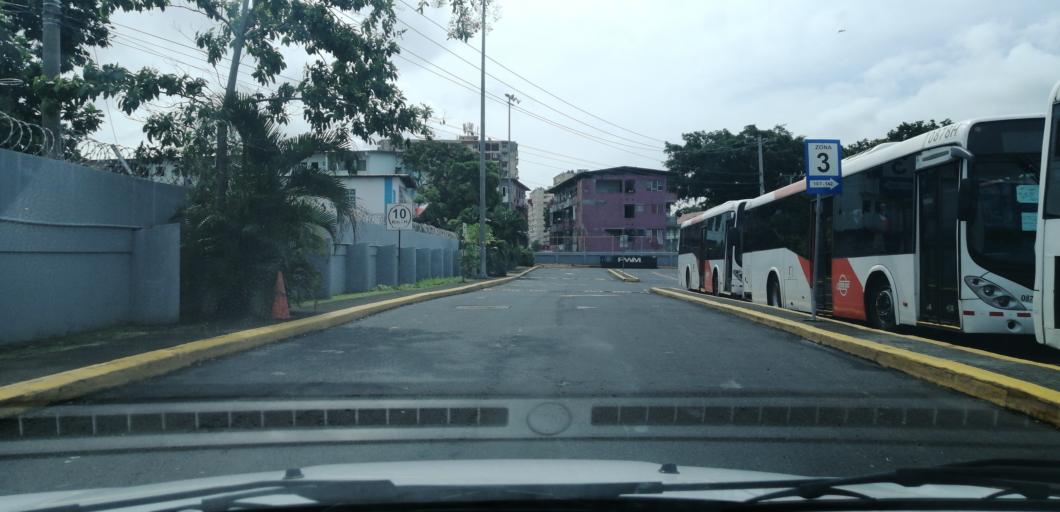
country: PA
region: Panama
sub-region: Distrito de Panama
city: Ancon
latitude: 8.9496
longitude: -79.5445
